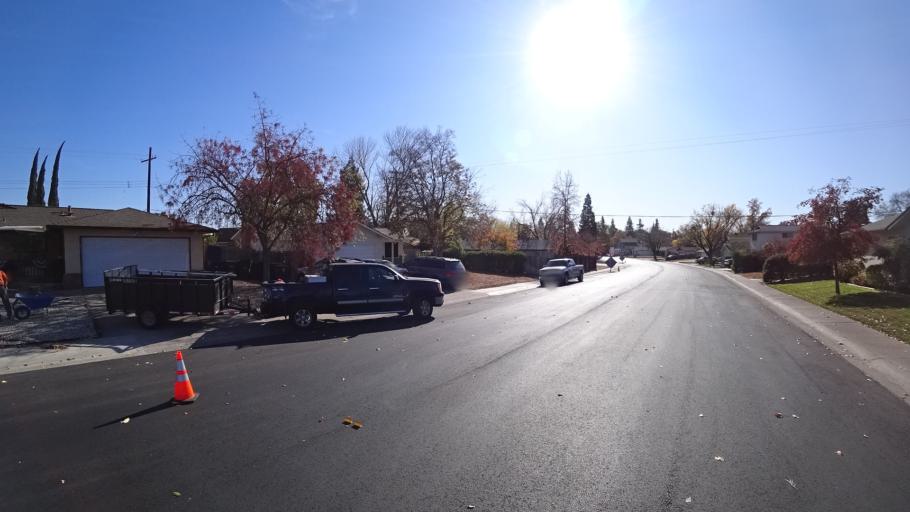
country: US
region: California
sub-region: Sacramento County
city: Antelope
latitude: 38.6860
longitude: -121.3134
